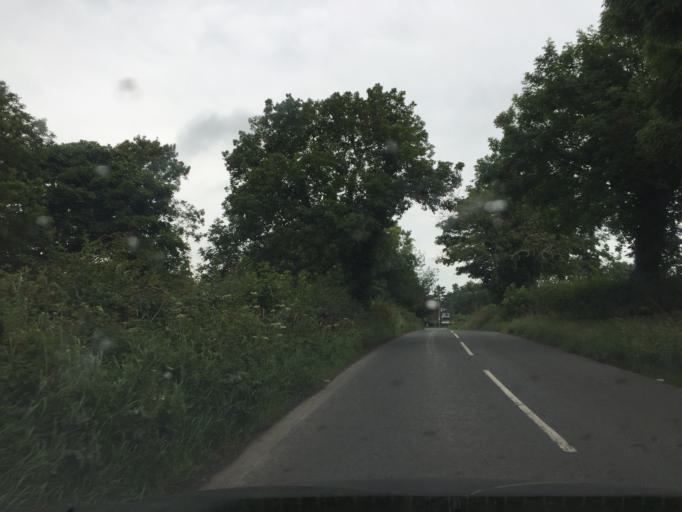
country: GB
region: Northern Ireland
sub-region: Down District
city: Kircubbin
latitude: 54.4929
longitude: -5.4996
